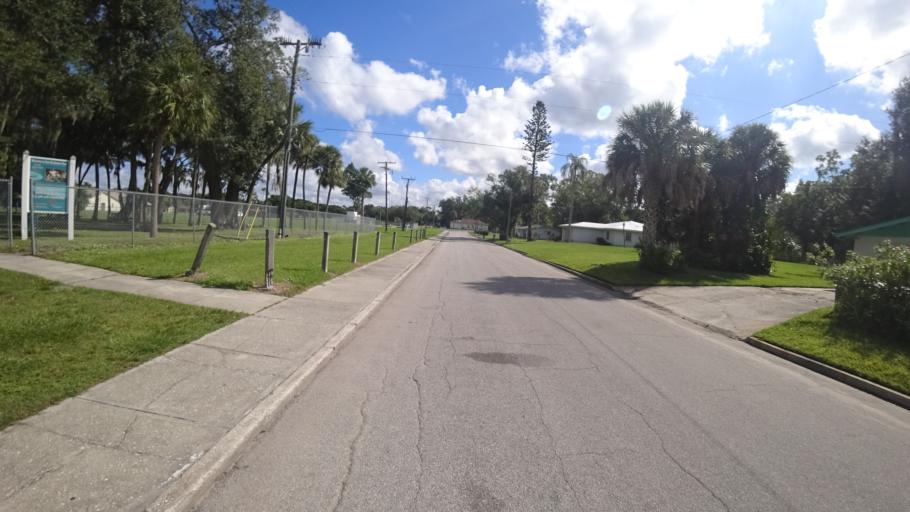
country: US
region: Florida
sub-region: Manatee County
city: Samoset
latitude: 27.4879
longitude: -82.5482
